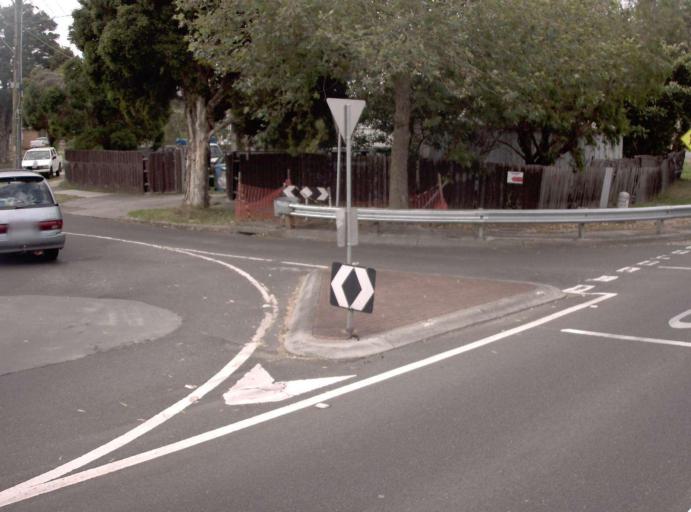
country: AU
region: Victoria
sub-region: Greater Dandenong
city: Dandenong North
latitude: -37.9630
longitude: 145.2248
